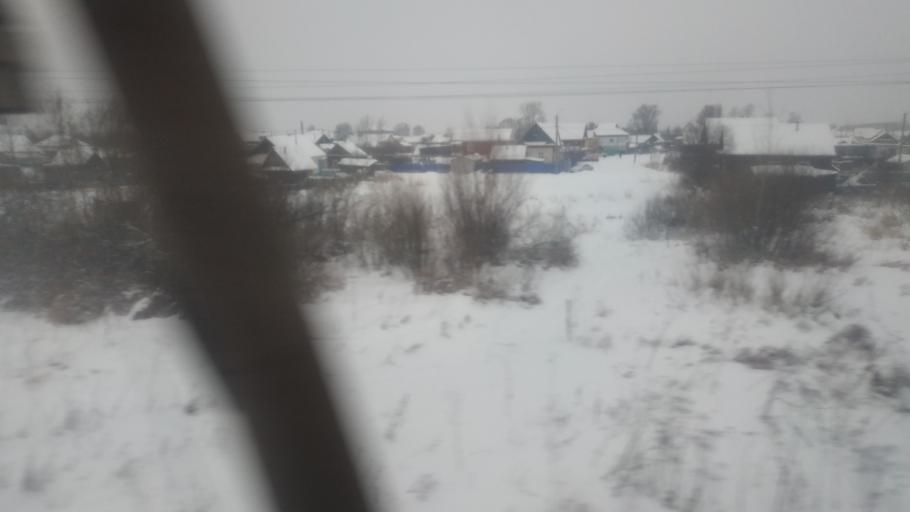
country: RU
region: Bashkortostan
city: Yanaul
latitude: 56.2778
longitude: 54.9481
